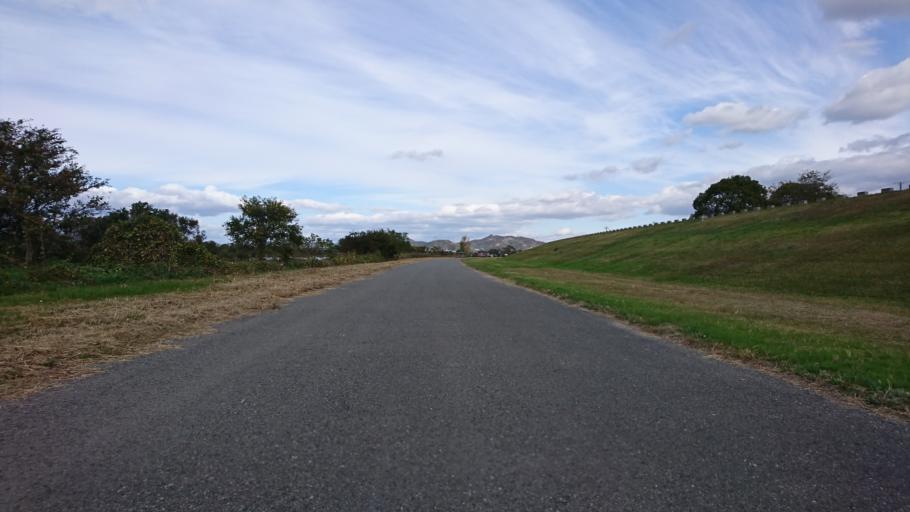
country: JP
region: Hyogo
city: Kakogawacho-honmachi
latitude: 34.7658
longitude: 134.8125
